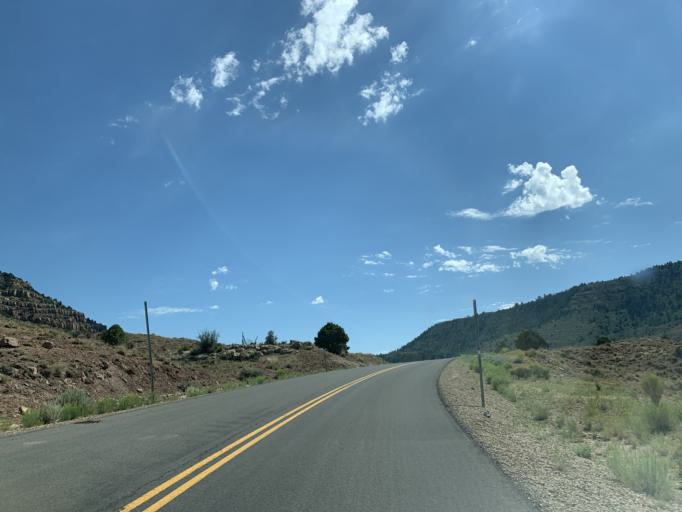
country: US
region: Utah
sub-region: Carbon County
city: East Carbon City
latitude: 39.7413
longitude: -110.5641
